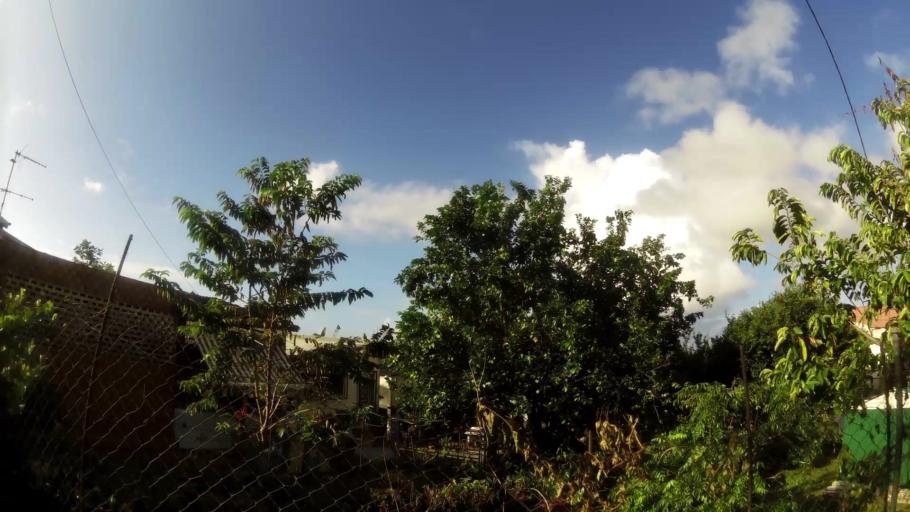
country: MQ
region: Martinique
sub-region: Martinique
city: Ducos
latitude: 14.5737
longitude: -60.9652
